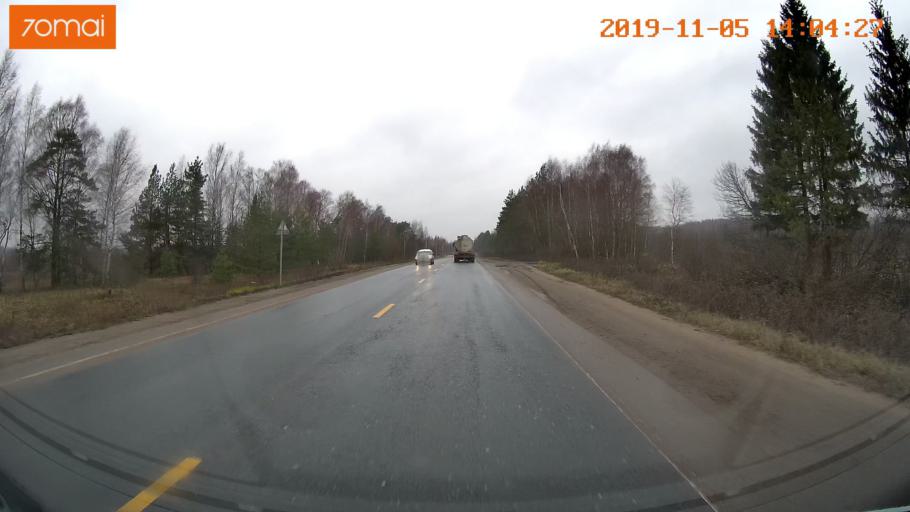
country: RU
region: Ivanovo
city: Kokhma
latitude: 56.9974
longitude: 41.1760
